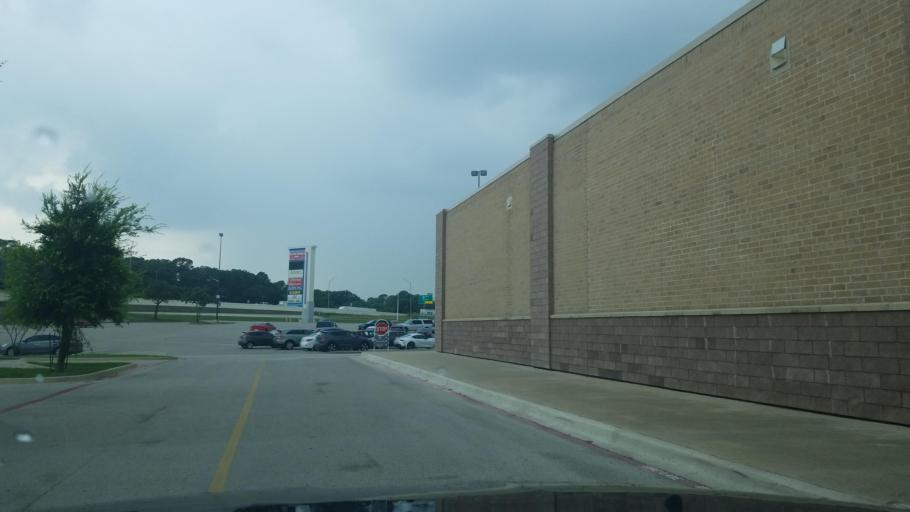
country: US
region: Texas
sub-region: Denton County
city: Denton
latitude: 33.1891
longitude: -97.1079
